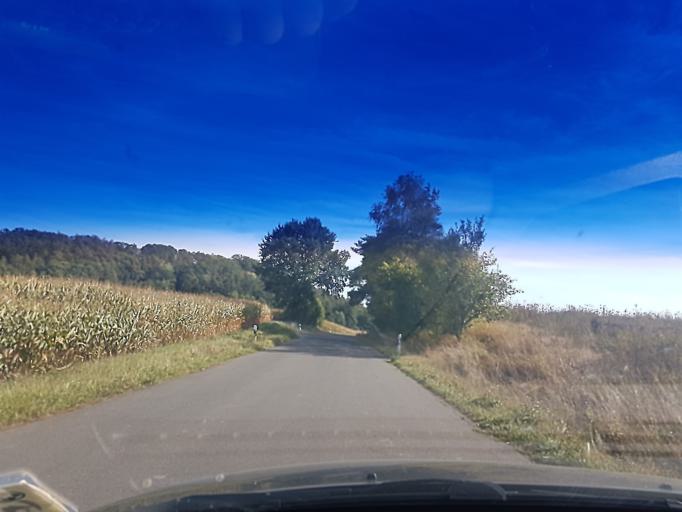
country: DE
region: Bavaria
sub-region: Upper Franconia
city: Schlusselfeld
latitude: 49.7756
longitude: 10.6023
